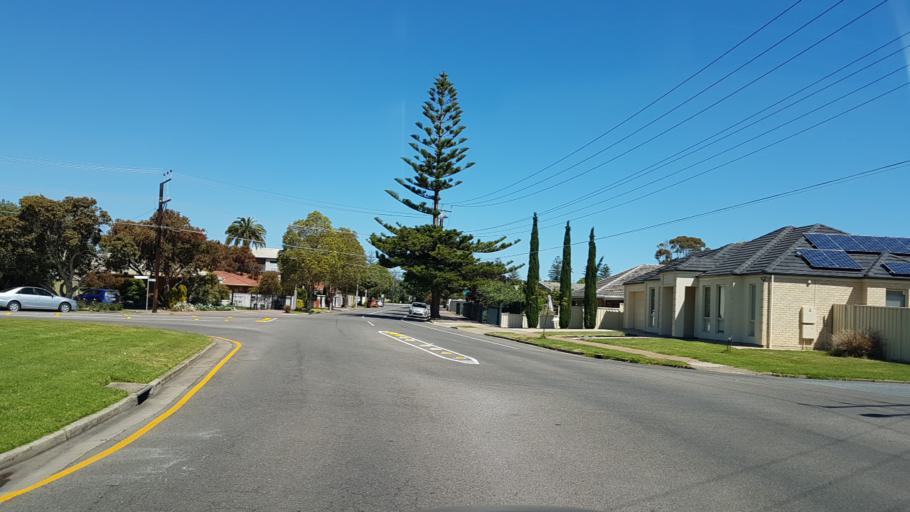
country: AU
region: South Australia
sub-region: Holdfast Bay
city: Glenelg East
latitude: -34.9742
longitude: 138.5287
